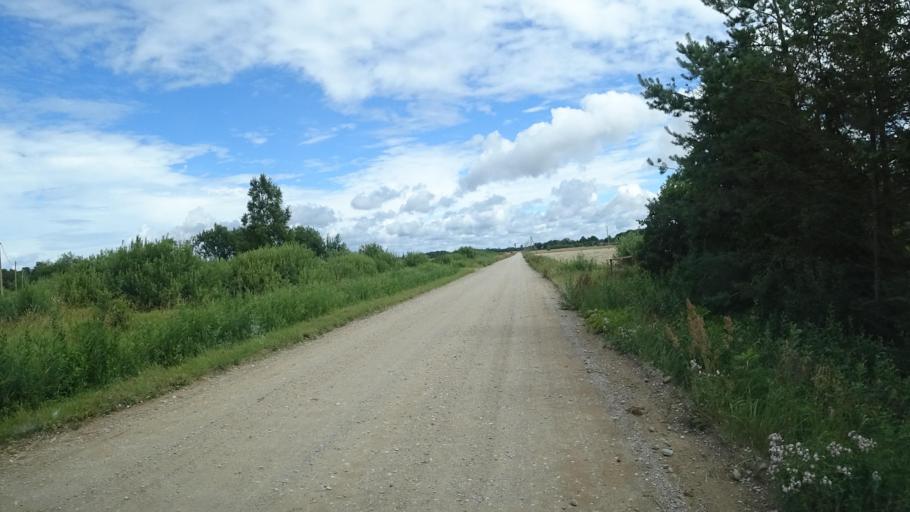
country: LV
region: Liepaja
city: Vec-Liepaja
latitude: 56.6497
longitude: 21.0470
